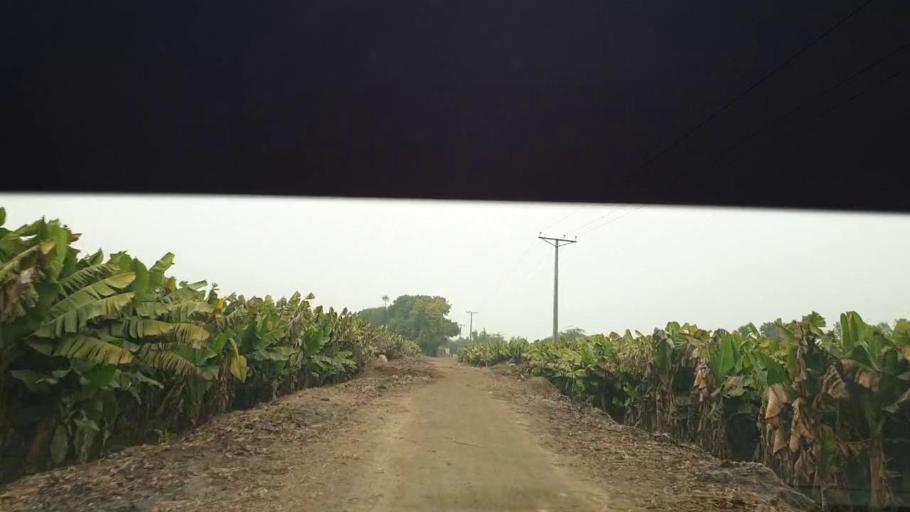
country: PK
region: Sindh
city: Berani
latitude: 25.7833
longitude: 68.7346
